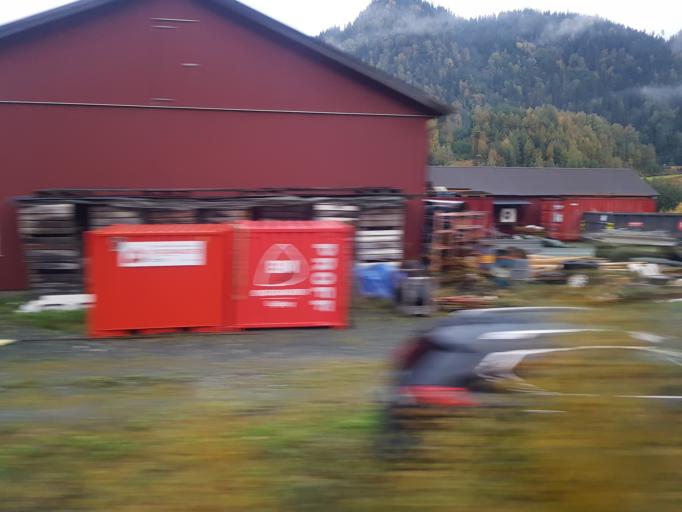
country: NO
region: Sor-Trondelag
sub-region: Midtre Gauldal
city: Storen
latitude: 63.0714
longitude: 10.2719
